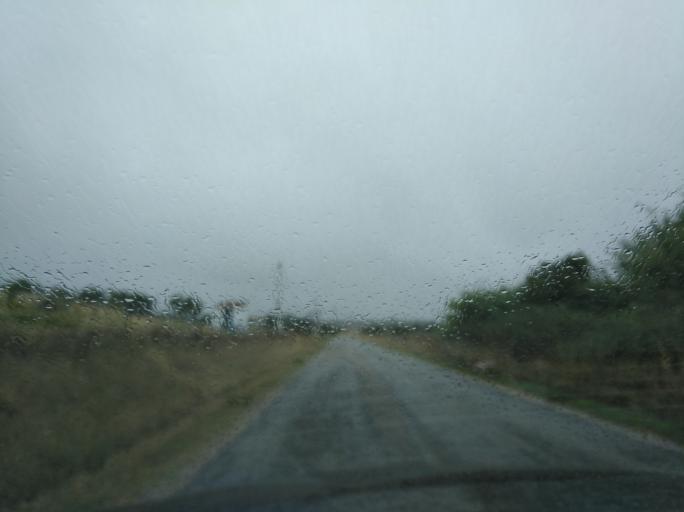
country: PT
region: Portalegre
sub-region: Campo Maior
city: Campo Maior
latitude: 38.9785
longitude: -7.0693
